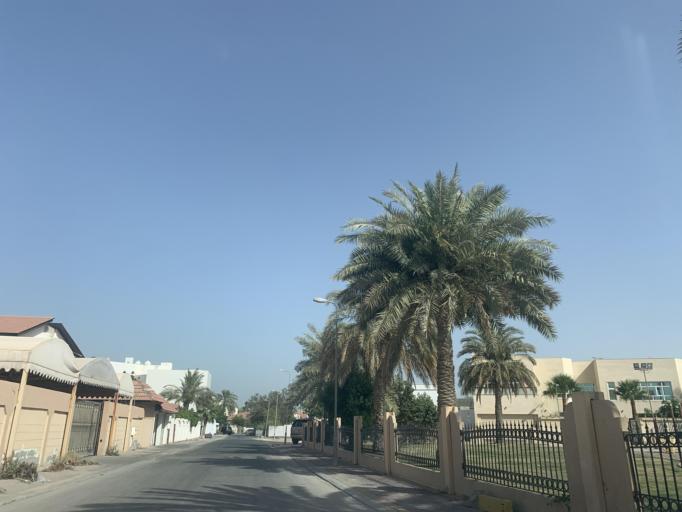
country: BH
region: Northern
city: Madinat `Isa
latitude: 26.1675
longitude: 50.5724
